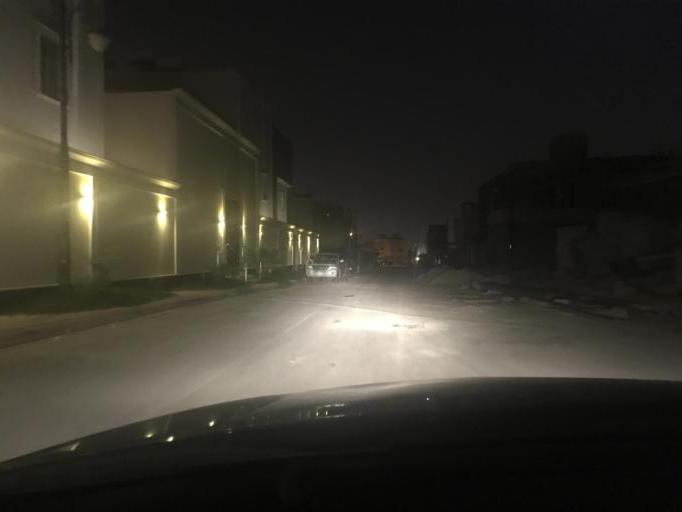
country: SA
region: Ar Riyad
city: Riyadh
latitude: 24.7378
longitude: 46.7848
